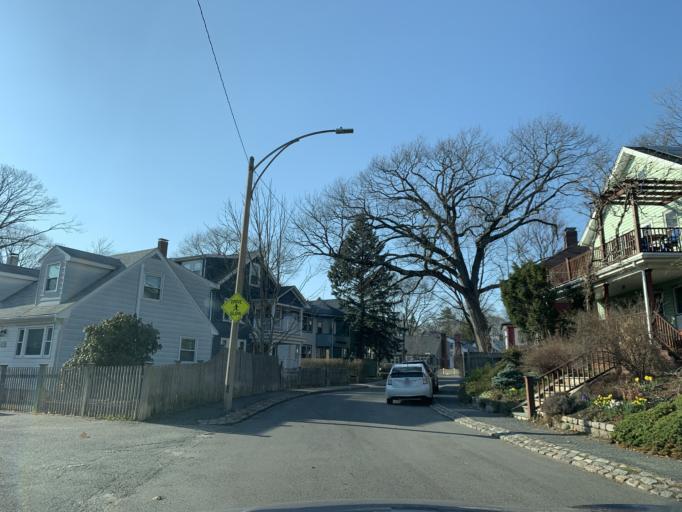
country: US
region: Massachusetts
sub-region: Suffolk County
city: Jamaica Plain
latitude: 42.2892
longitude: -71.1137
